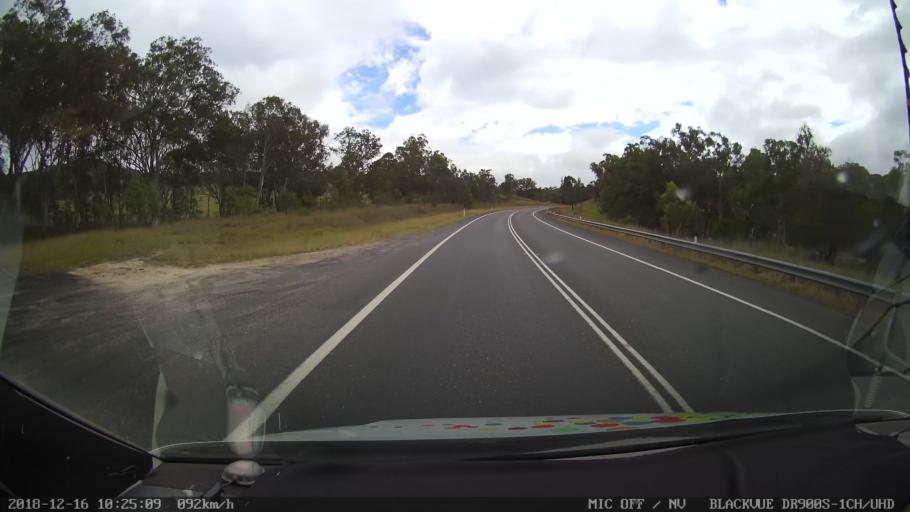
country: AU
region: New South Wales
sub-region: Tenterfield Municipality
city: Carrolls Creek
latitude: -29.1624
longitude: 152.0008
